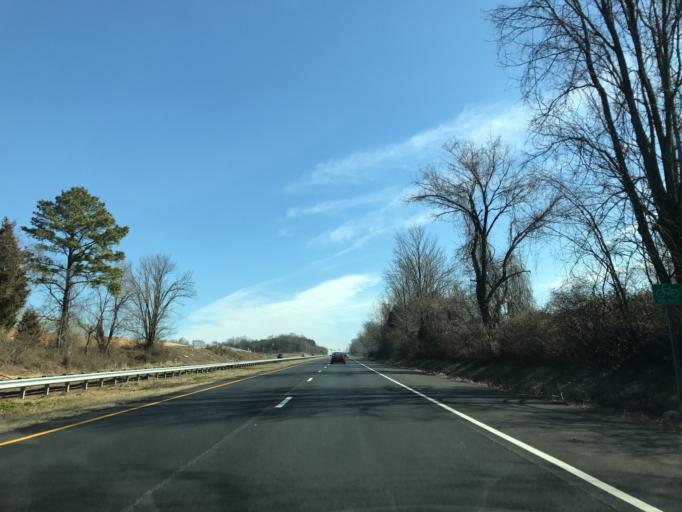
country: US
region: Maryland
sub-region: Cecil County
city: Perryville
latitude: 39.5811
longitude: -76.0292
